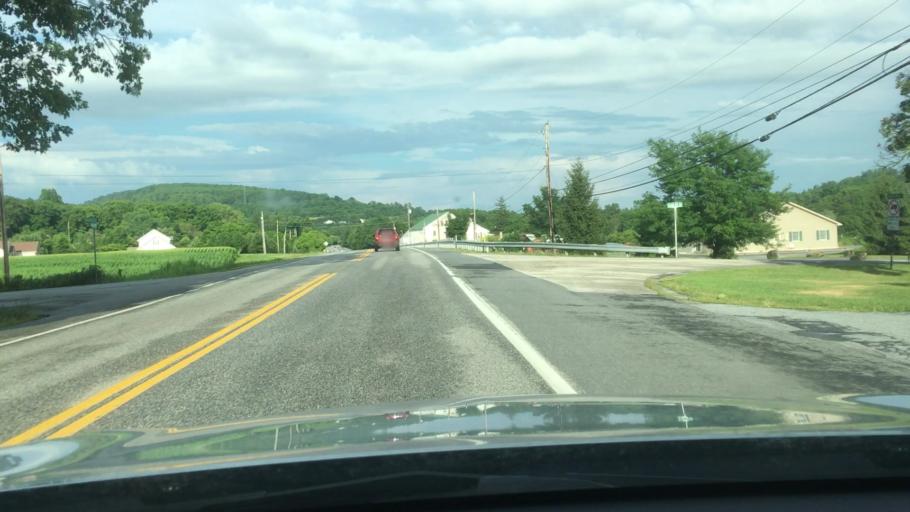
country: US
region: Pennsylvania
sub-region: York County
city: Dillsburg
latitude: 40.1013
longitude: -76.9939
